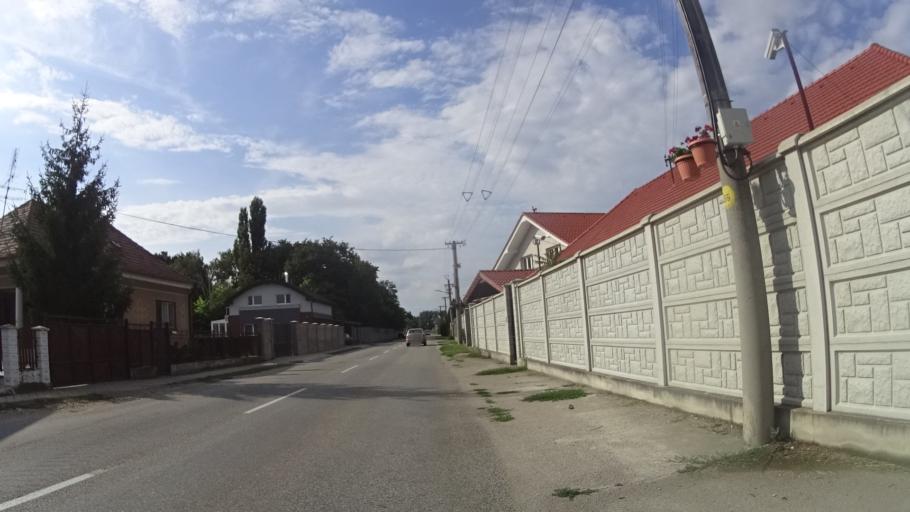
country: SK
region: Trnavsky
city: Gabcikovo
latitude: 47.9218
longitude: 17.4974
